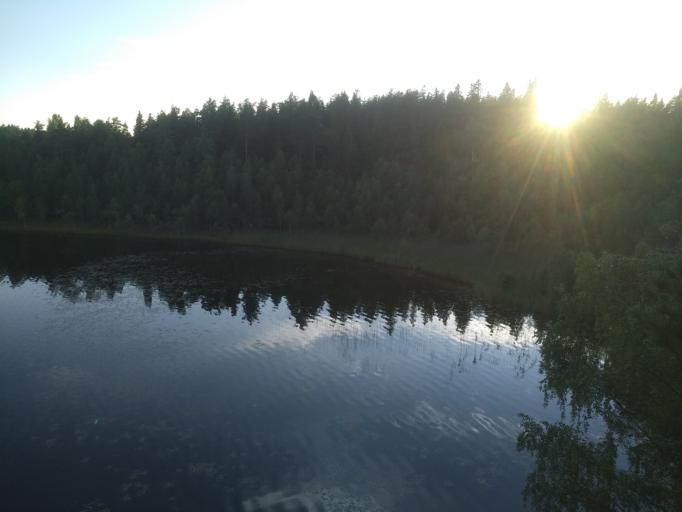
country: RU
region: Leningrad
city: Kuznechnoye
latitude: 61.1645
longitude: 29.7234
